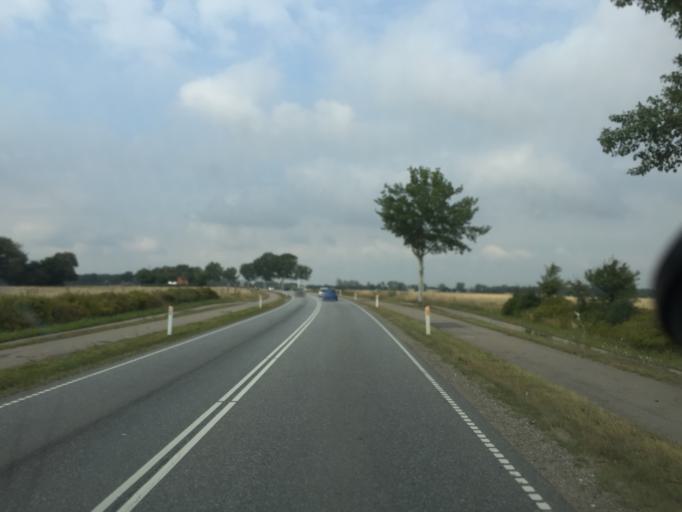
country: DK
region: Zealand
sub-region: Solrod Kommune
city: Solrod
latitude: 55.5373
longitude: 12.1775
